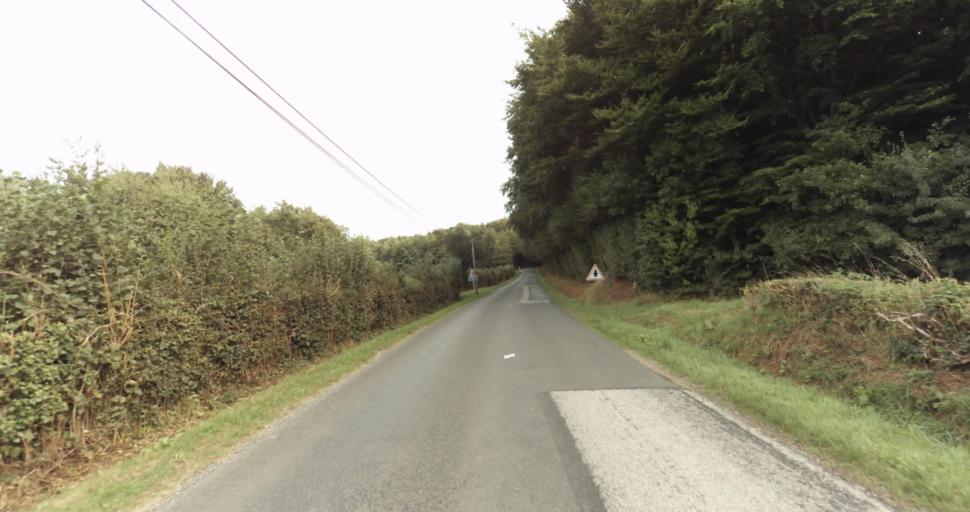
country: FR
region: Lower Normandy
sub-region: Departement de l'Orne
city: Gace
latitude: 48.8199
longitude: 0.2335
